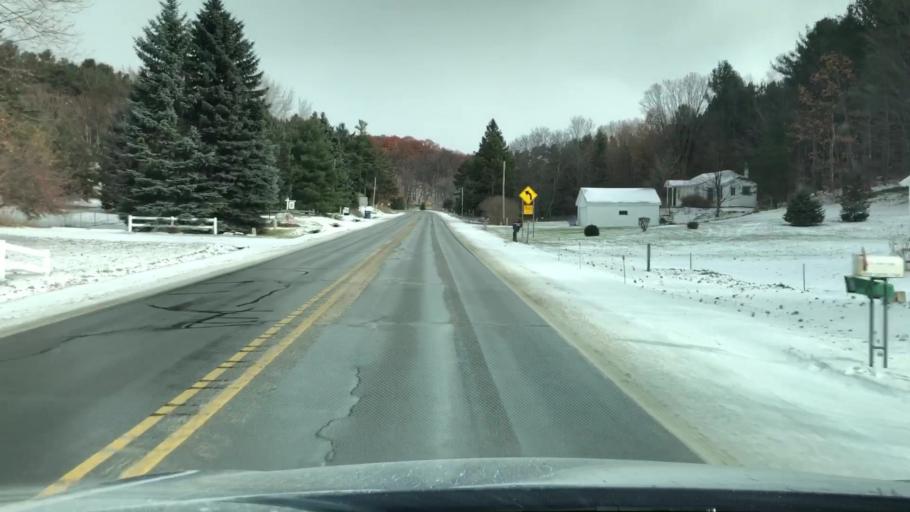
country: US
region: Michigan
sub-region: Grand Traverse County
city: Traverse City
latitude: 44.8406
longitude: -85.5336
